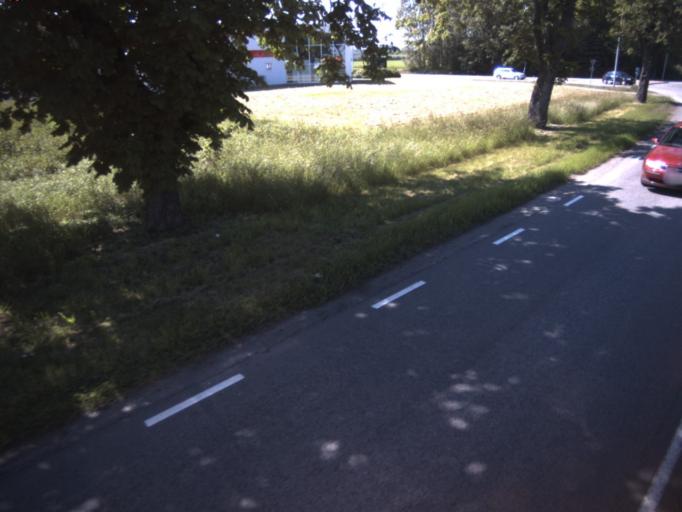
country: SE
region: Skane
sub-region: Helsingborg
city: Barslov
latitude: 56.0437
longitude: 12.7783
